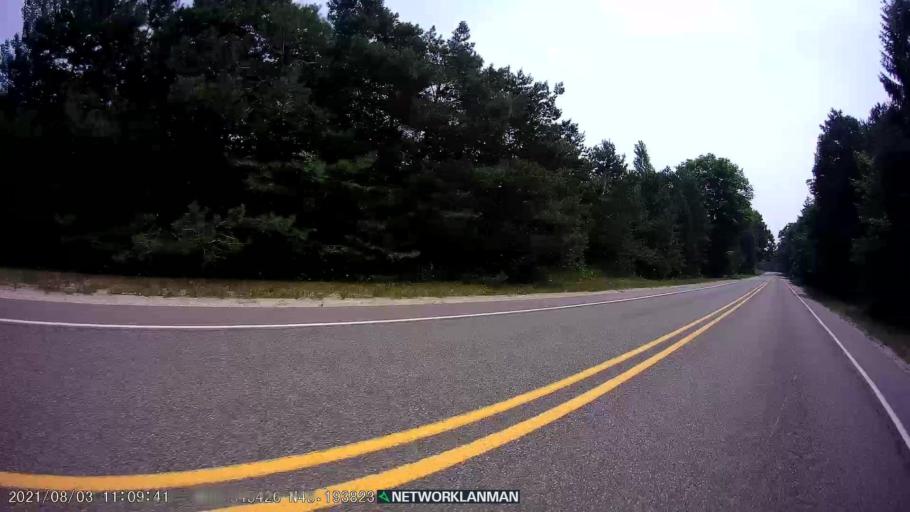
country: US
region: Michigan
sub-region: Leelanau County
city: Leland
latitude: 45.1936
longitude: -85.5455
